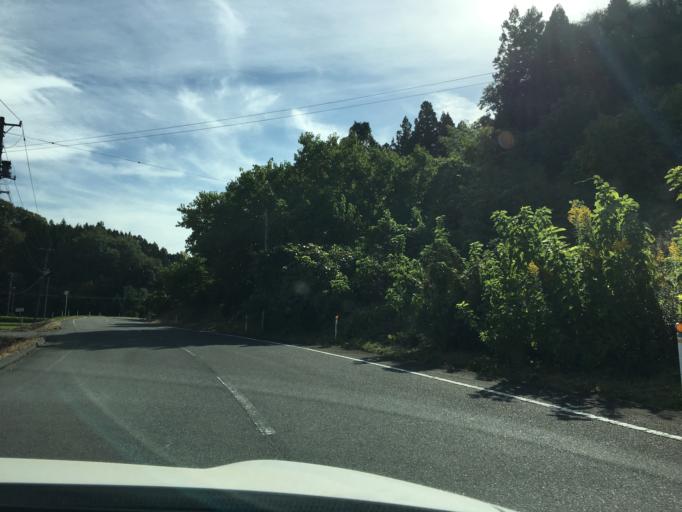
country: JP
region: Fukushima
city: Miharu
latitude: 37.4820
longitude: 140.4961
